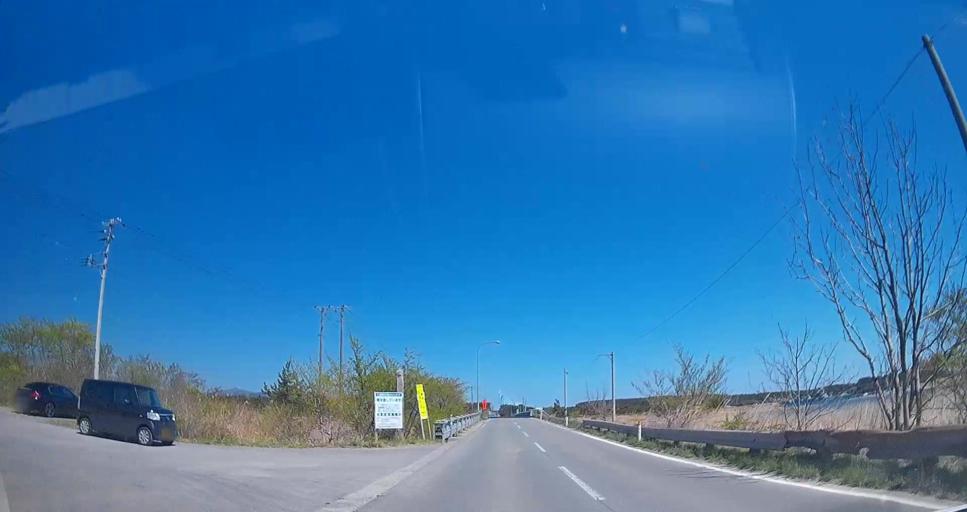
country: JP
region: Aomori
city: Misawa
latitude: 40.9302
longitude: 141.3745
